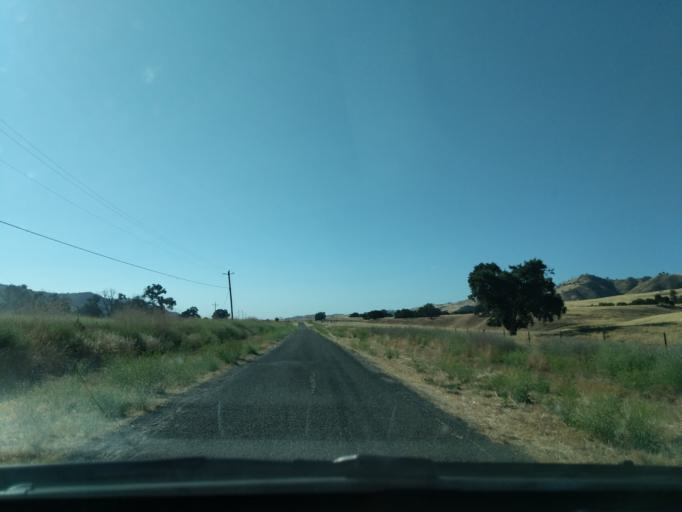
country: US
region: California
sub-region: Monterey County
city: King City
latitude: 36.1497
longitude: -120.7597
